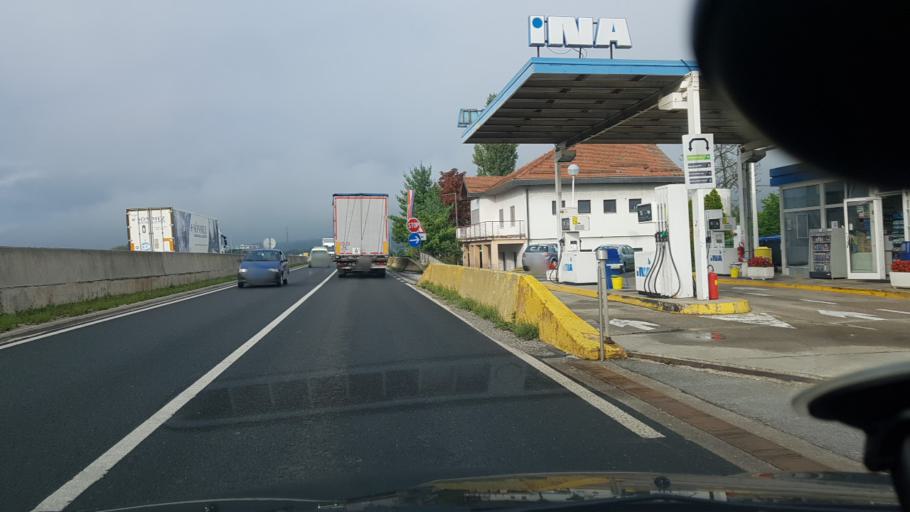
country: HR
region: Krapinsko-Zagorska
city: Oroslavje
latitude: 46.0059
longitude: 15.8728
